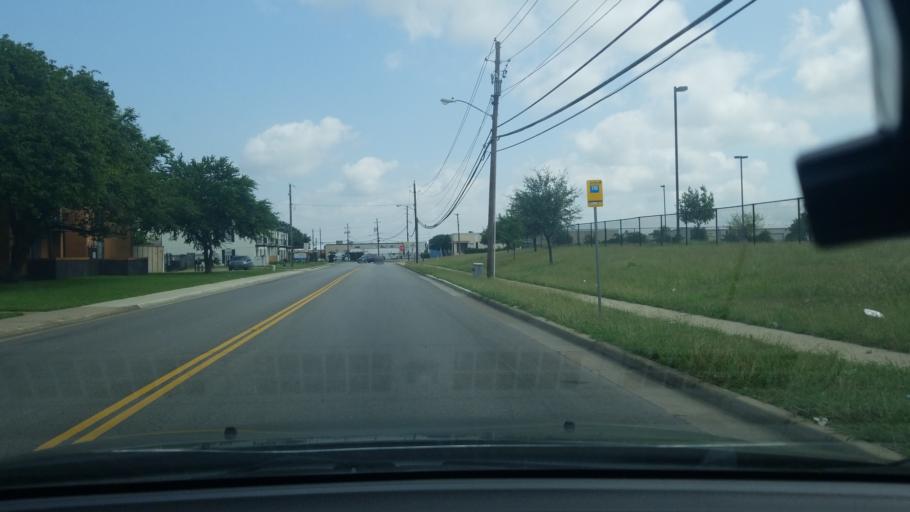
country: US
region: Texas
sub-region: Dallas County
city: Mesquite
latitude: 32.8015
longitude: -96.6882
